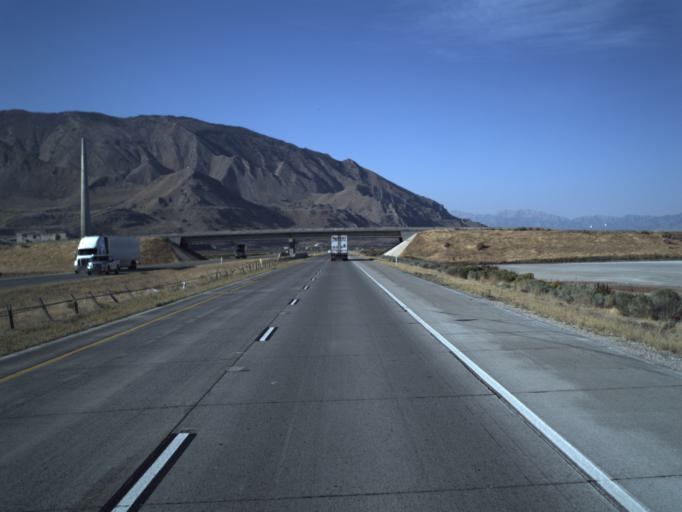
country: US
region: Utah
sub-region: Salt Lake County
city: Magna
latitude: 40.7472
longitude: -112.1810
